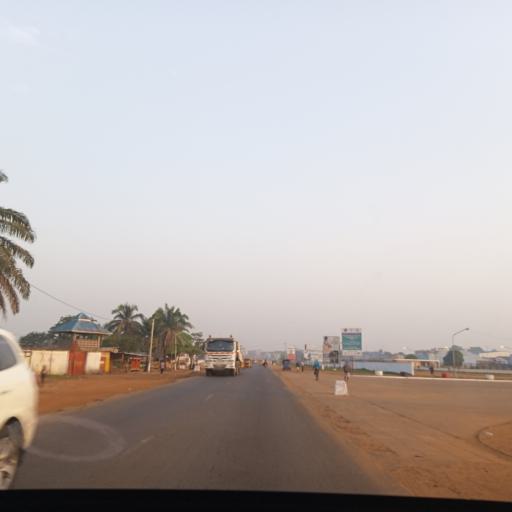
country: LR
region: Montserrado
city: Monrovia
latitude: 6.2562
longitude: -10.7042
